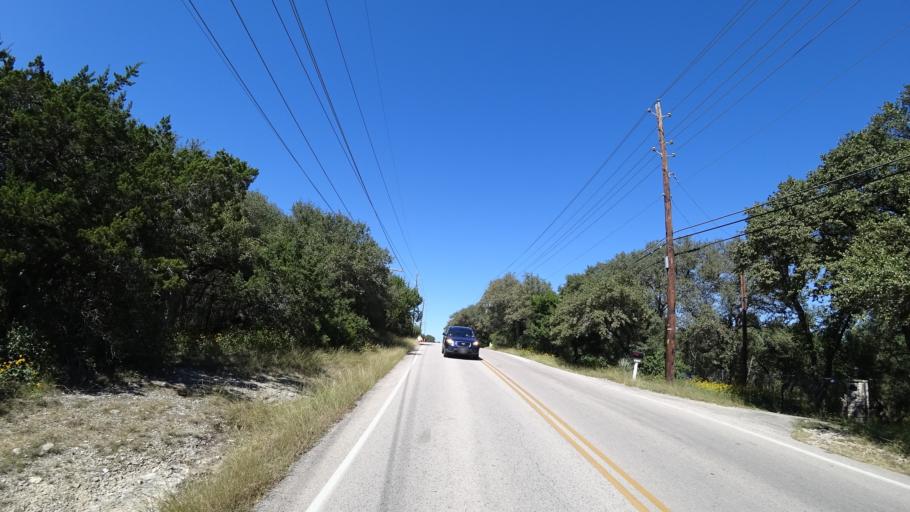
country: US
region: Texas
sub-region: Travis County
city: West Lake Hills
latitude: 30.3247
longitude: -97.7796
